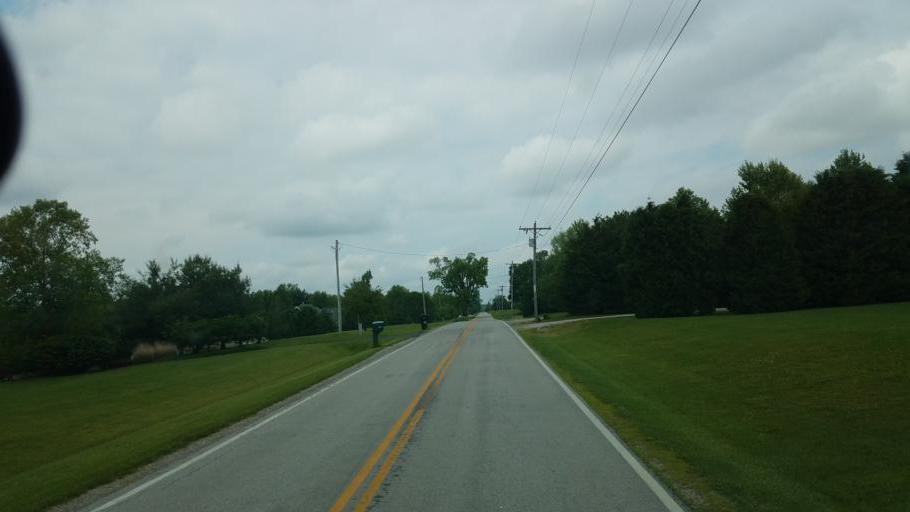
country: US
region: Ohio
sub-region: Marion County
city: Prospect
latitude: 40.3514
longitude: -83.1783
